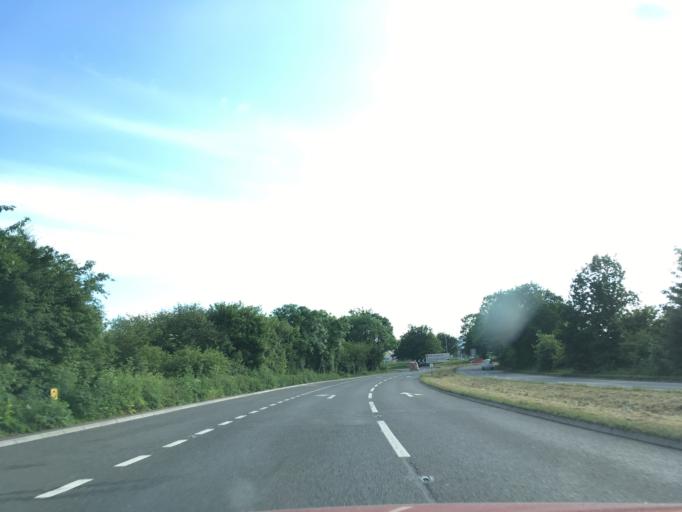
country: GB
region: England
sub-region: Somerset
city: Puriton
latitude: 51.1655
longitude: -2.9864
